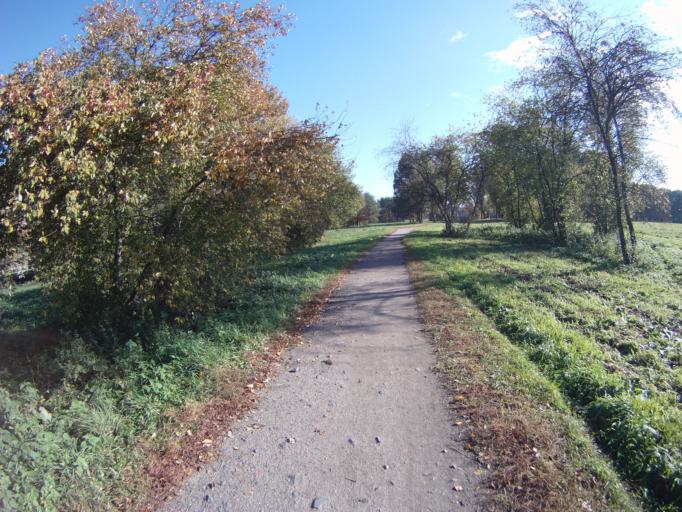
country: BY
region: Minsk
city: Minsk
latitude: 53.9362
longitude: 27.5698
